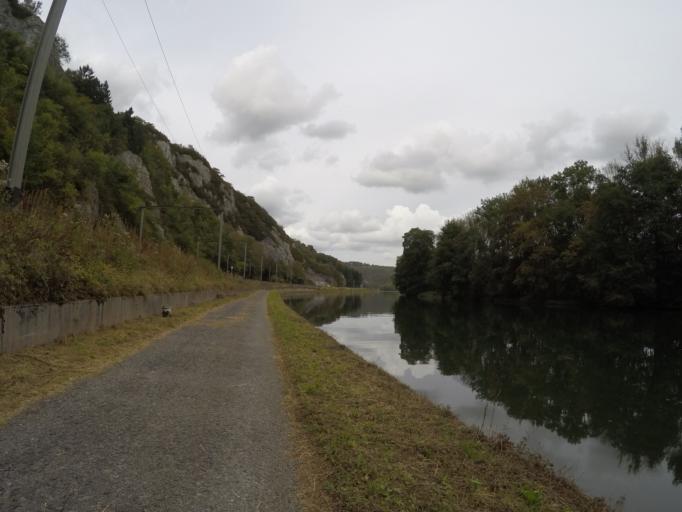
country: BE
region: Wallonia
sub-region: Province de Namur
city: Anhee
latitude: 50.2870
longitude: 4.8909
